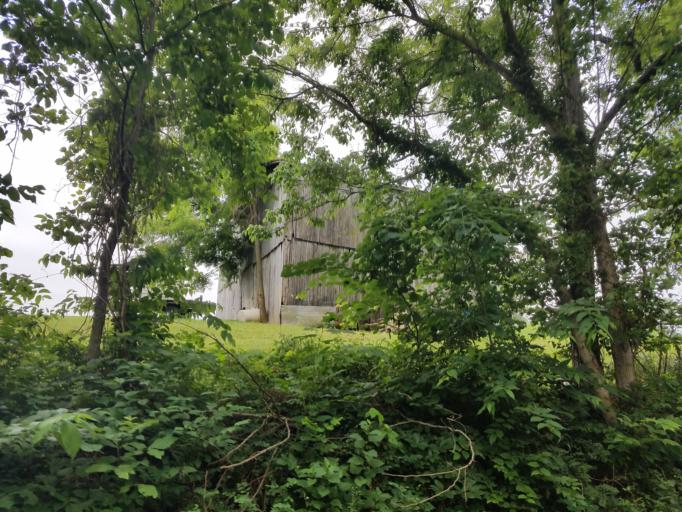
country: US
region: Kentucky
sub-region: Mercer County
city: Jackson
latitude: 37.8126
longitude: -85.0519
